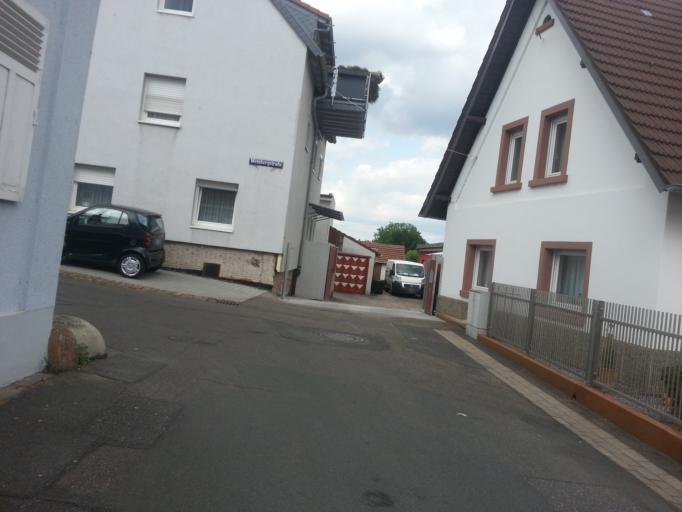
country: DE
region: Baden-Wuerttemberg
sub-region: Karlsruhe Region
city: Ilvesheim
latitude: 49.4886
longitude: 8.5349
